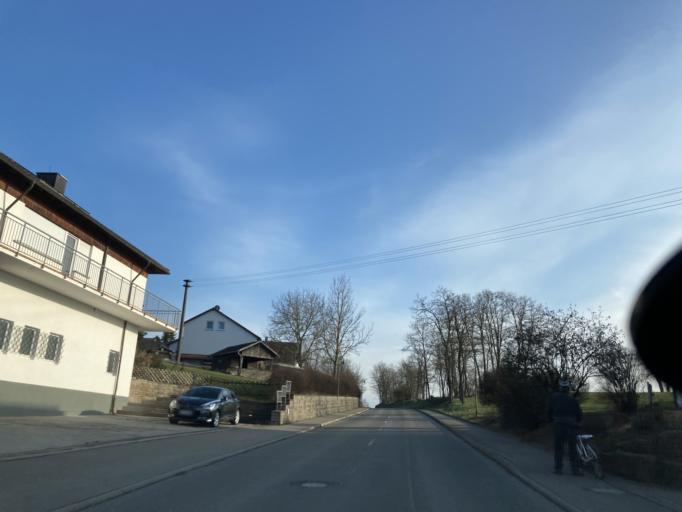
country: DE
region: Baden-Wuerttemberg
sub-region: Tuebingen Region
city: Hirrlingen
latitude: 48.4041
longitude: 8.8835
